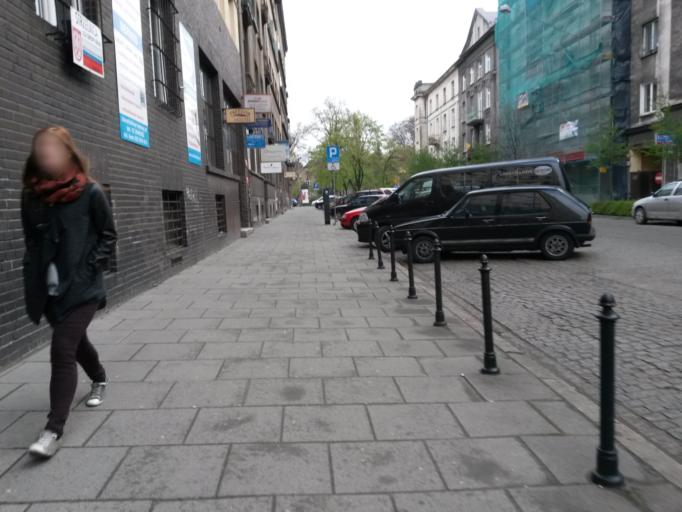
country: PL
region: Lesser Poland Voivodeship
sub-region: Krakow
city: Krakow
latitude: 50.0706
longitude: 19.9250
